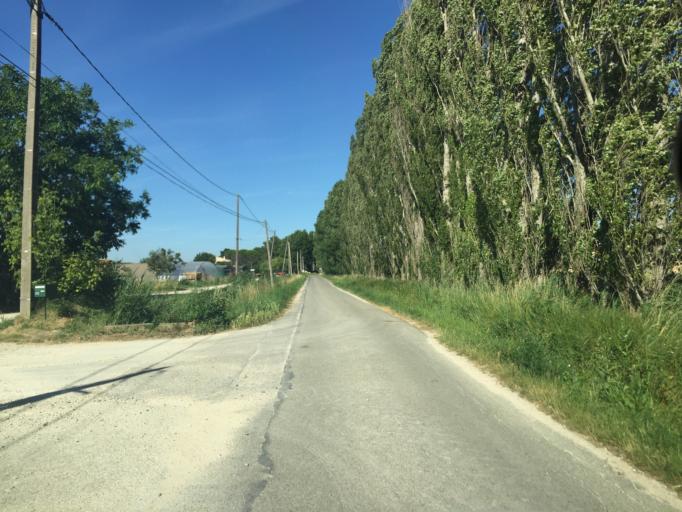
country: FR
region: Provence-Alpes-Cote d'Azur
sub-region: Departement du Vaucluse
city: Caderousse
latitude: 44.1189
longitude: 4.7667
